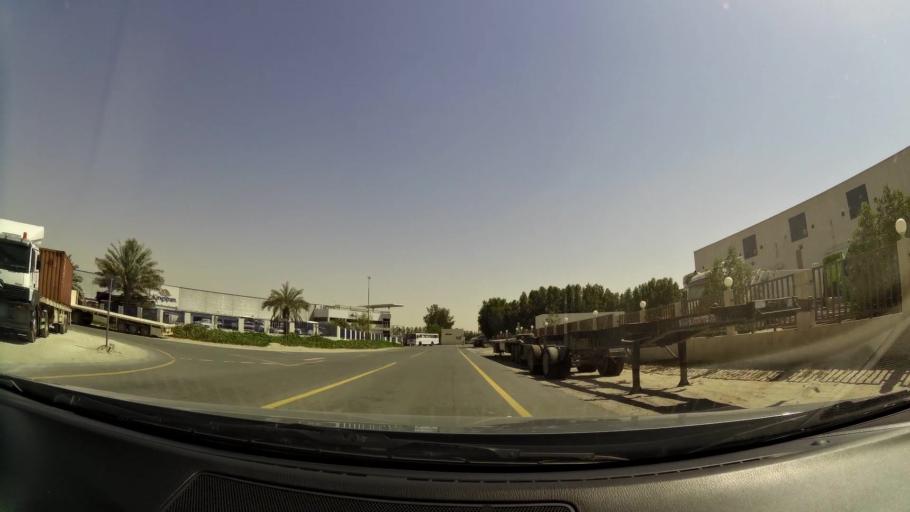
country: AE
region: Dubai
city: Dubai
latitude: 24.9680
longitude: 55.1783
